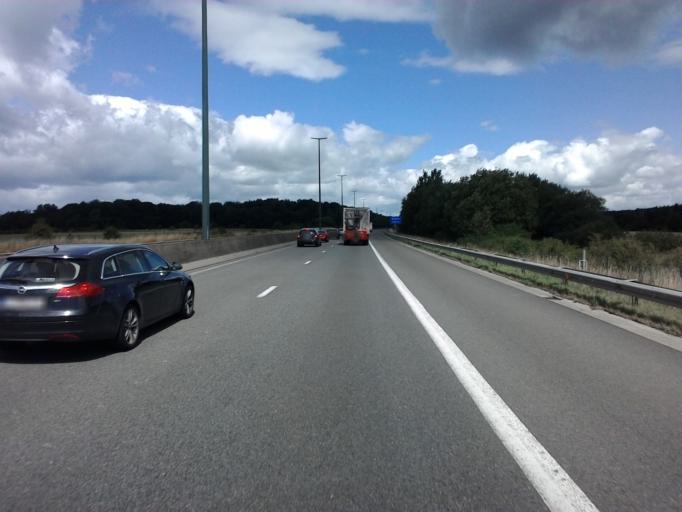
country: BE
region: Wallonia
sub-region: Province du Luxembourg
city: Habay-la-Vieille
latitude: 49.7290
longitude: 5.5817
